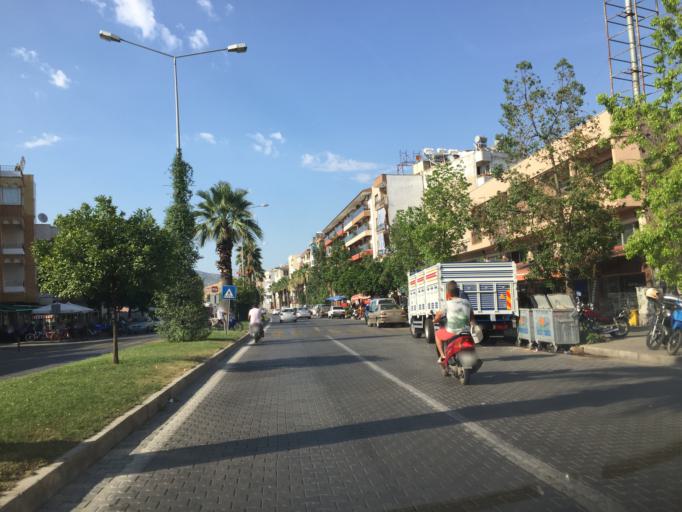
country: TR
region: Izmir
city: Selcuk
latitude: 37.9515
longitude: 27.3703
